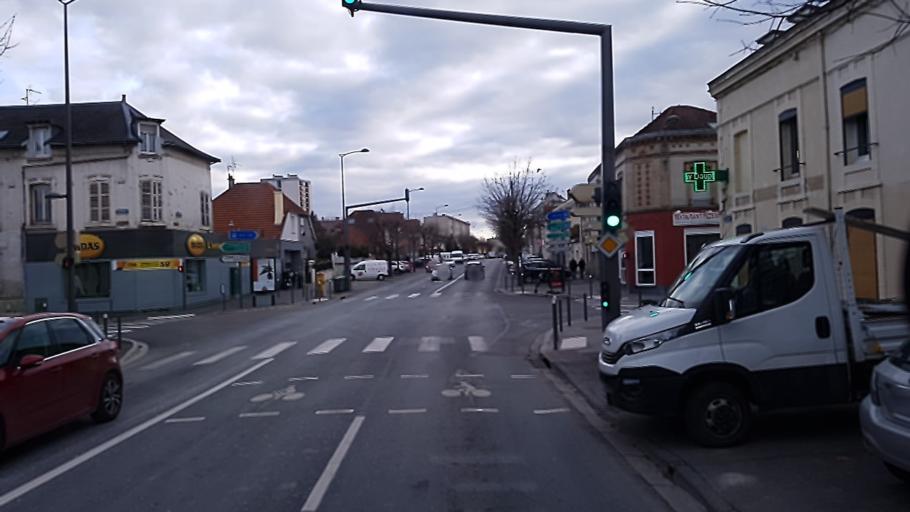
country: FR
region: Champagne-Ardenne
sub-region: Departement de la Marne
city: Reims
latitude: 49.2582
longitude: 4.0561
